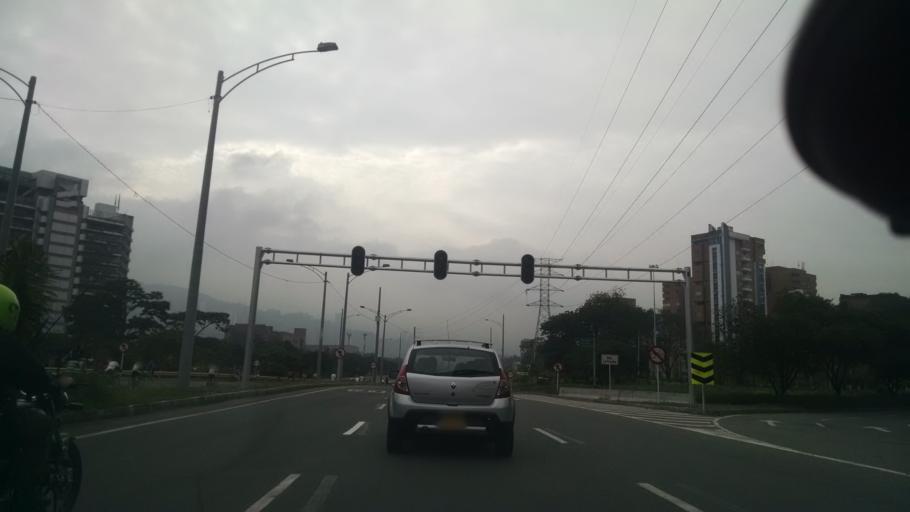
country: CO
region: Antioquia
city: Medellin
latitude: 6.2469
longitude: -75.5805
